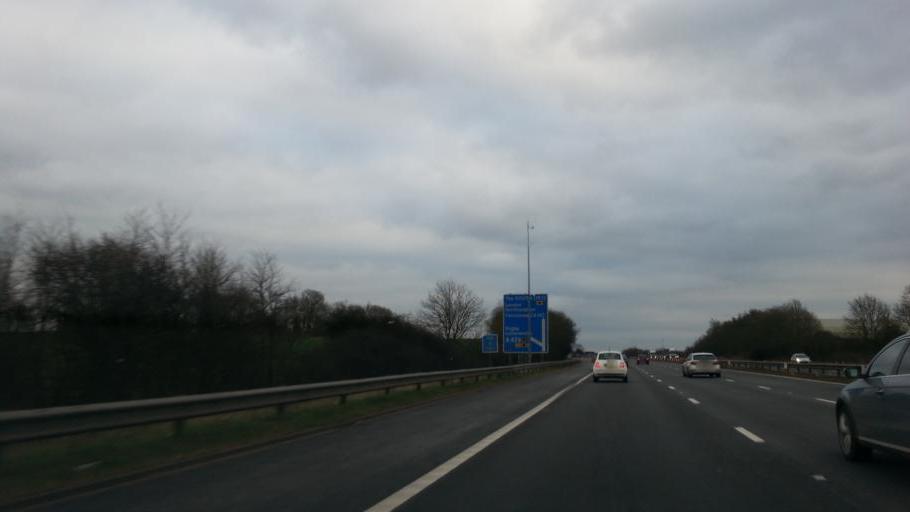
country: GB
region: England
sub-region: Warwickshire
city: Rugby
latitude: 52.4098
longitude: -1.2580
